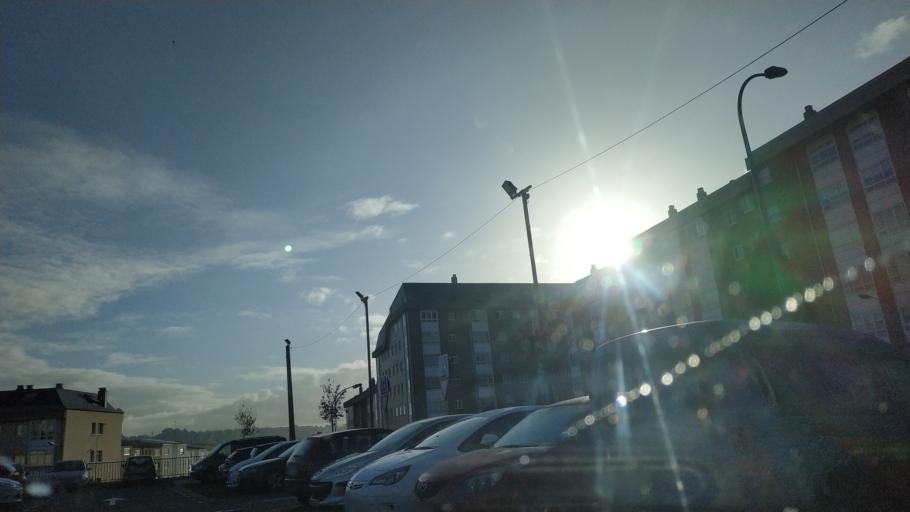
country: ES
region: Galicia
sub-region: Provincia da Coruna
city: Culleredo
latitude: 43.3261
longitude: -8.3842
